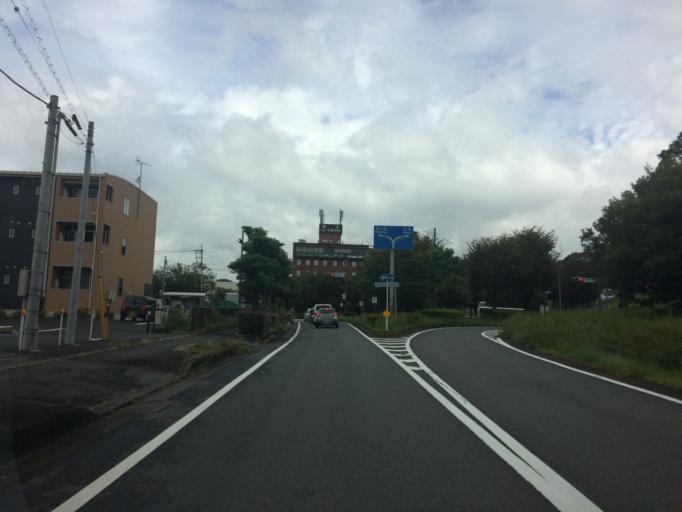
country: JP
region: Shizuoka
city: Fuji
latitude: 35.1721
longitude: 138.6729
